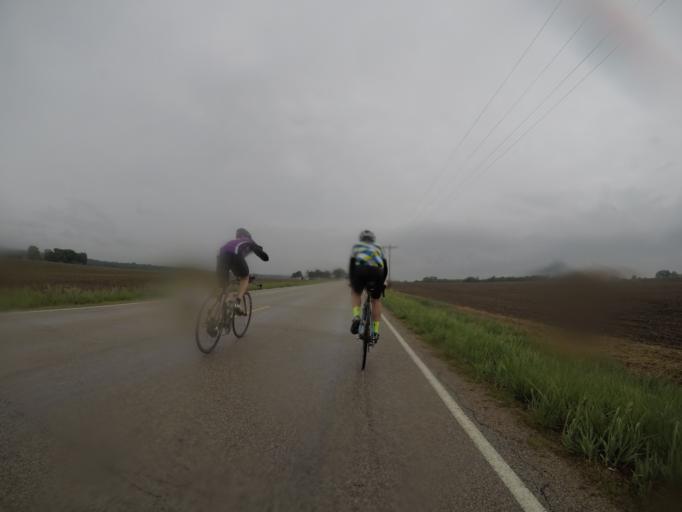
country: US
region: Kansas
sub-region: Pottawatomie County
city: Wamego
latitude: 39.3260
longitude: -96.2214
